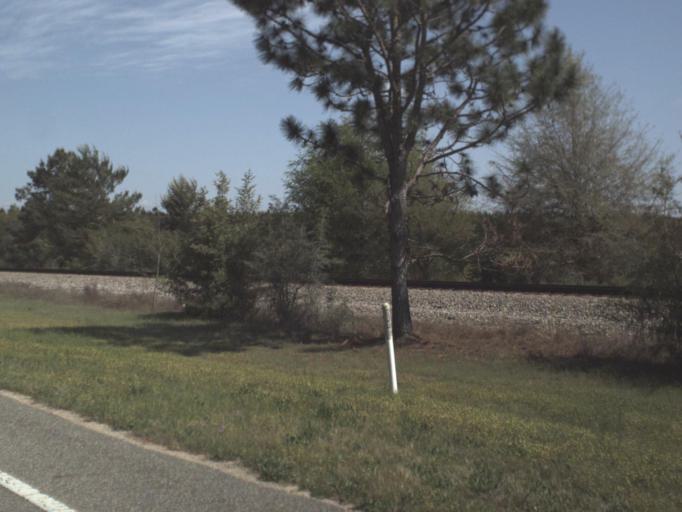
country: US
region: Florida
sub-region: Okaloosa County
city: Crestview
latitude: 30.7504
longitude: -86.4629
